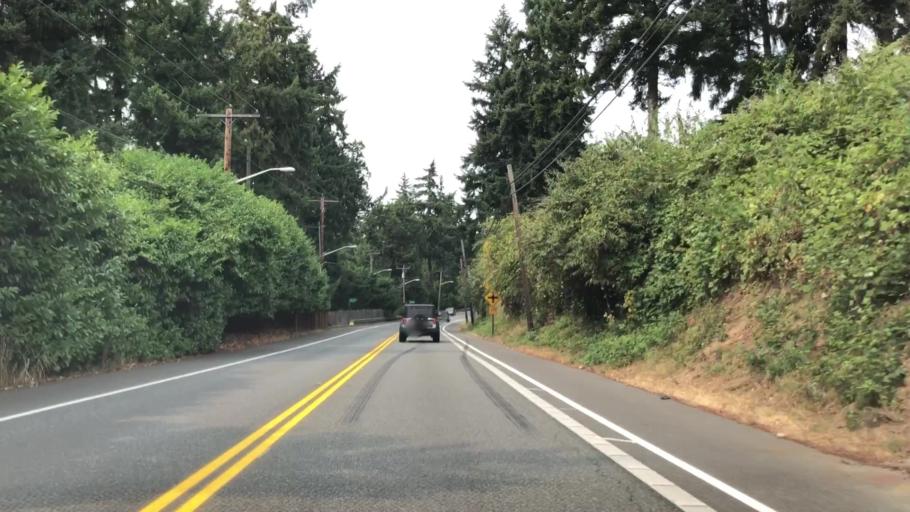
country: US
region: Washington
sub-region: King County
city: Inglewood-Finn Hill
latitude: 47.7000
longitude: -122.2338
